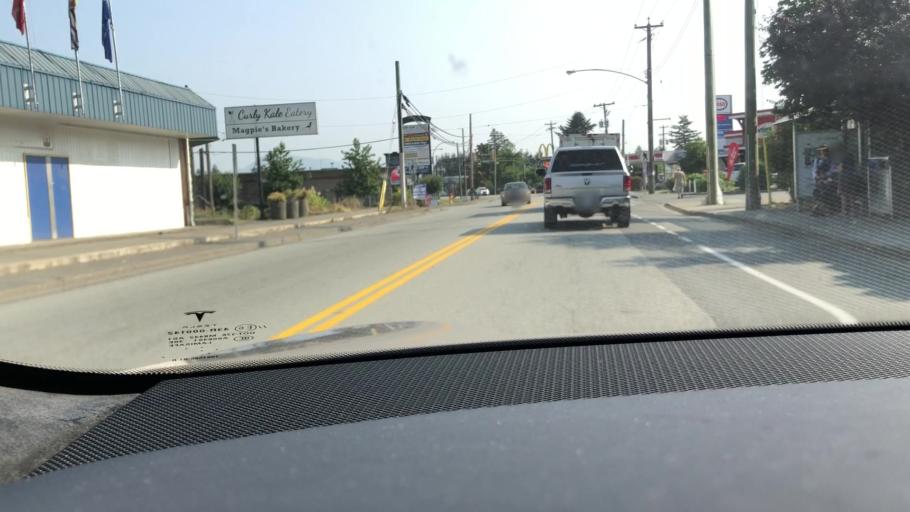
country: CA
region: British Columbia
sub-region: Fraser Valley Regional District
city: Chilliwack
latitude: 49.1056
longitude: -121.9614
